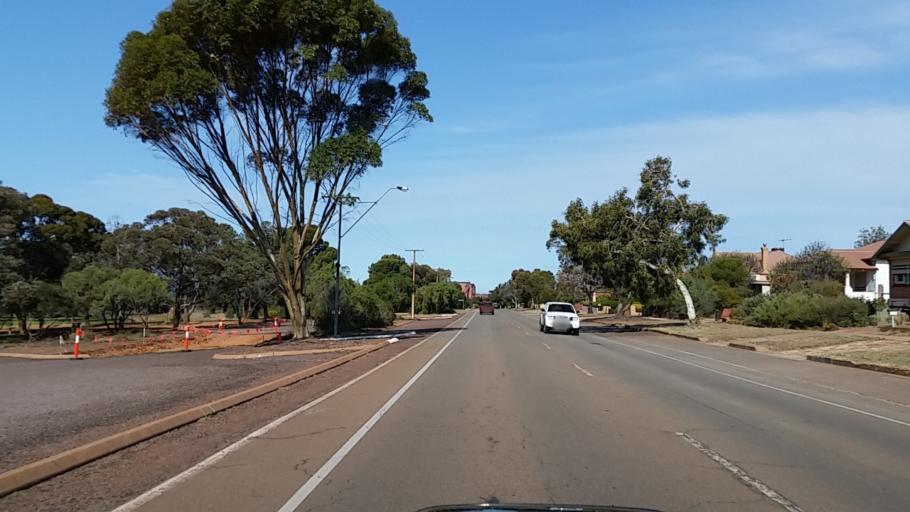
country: AU
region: South Australia
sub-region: Whyalla
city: Whyalla
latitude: -33.0263
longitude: 137.5743
